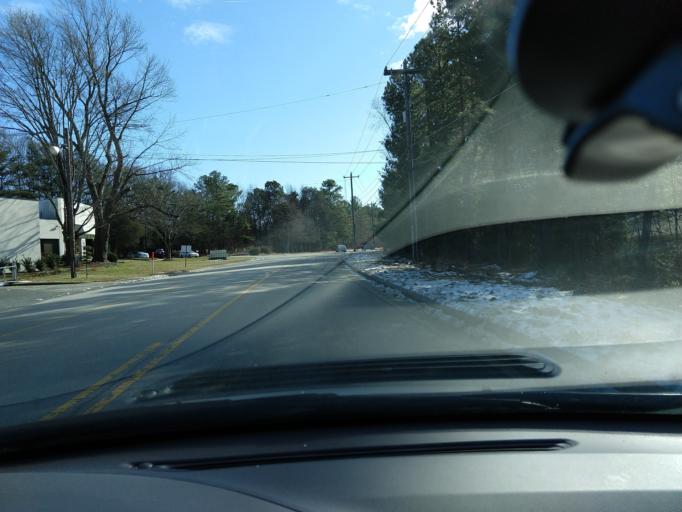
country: US
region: North Carolina
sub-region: Guilford County
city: Greensboro
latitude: 36.1254
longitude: -79.8444
